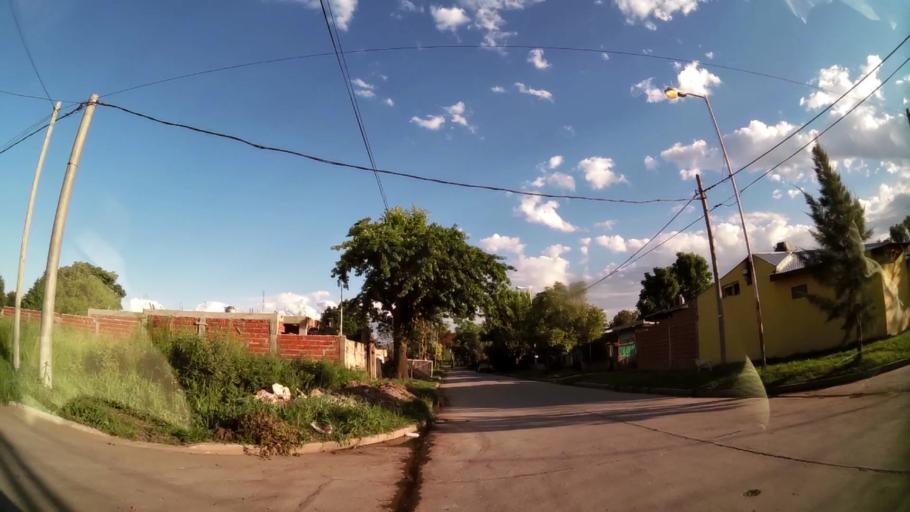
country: AR
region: Buenos Aires
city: Santa Catalina - Dique Lujan
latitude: -34.4733
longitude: -58.7496
